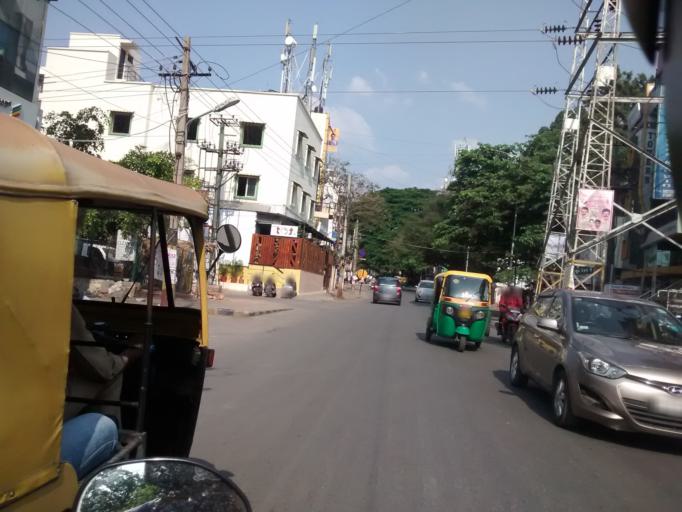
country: IN
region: Karnataka
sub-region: Bangalore Urban
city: Bangalore
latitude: 12.9682
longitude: 77.6513
